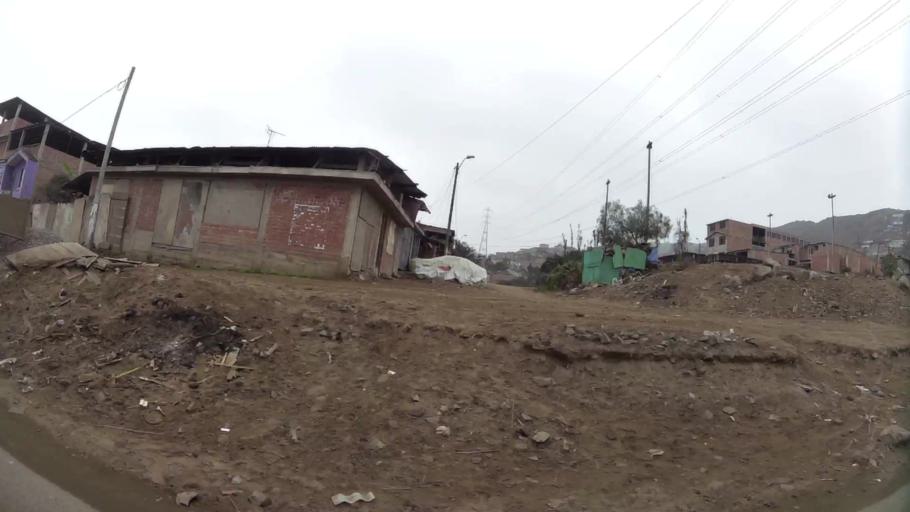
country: PE
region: Lima
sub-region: Lima
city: Surco
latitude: -12.2173
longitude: -76.9188
